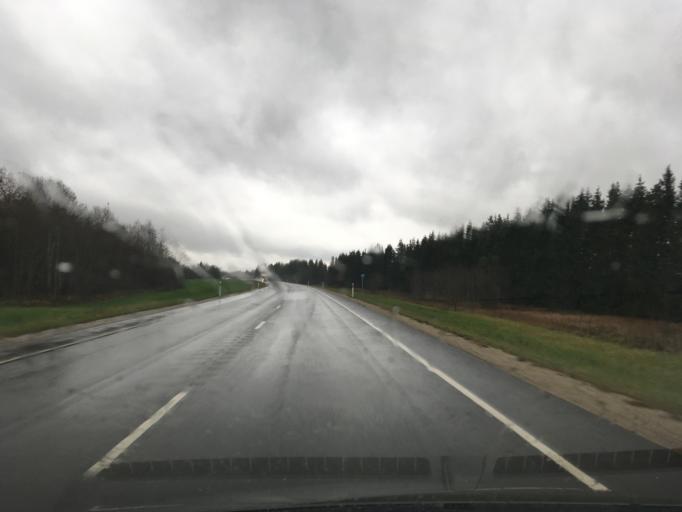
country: EE
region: Laeaene
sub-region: Lihula vald
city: Lihula
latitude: 58.7728
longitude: 23.9895
